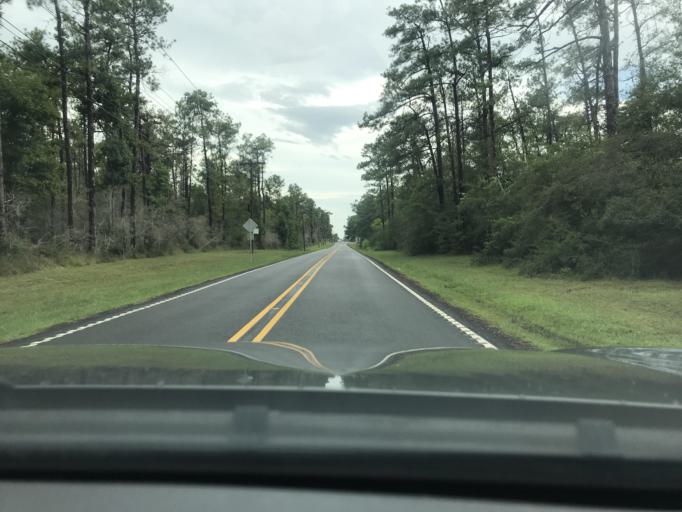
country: US
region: Louisiana
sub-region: Calcasieu Parish
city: Westlake
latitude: 30.3020
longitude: -93.2584
